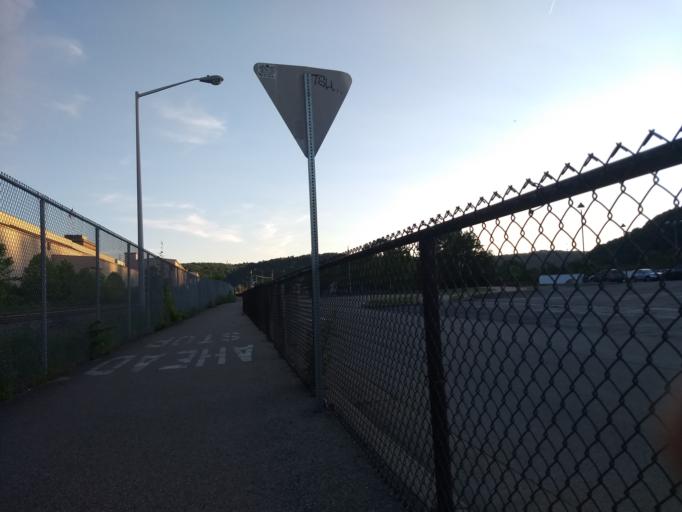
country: US
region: Pennsylvania
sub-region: Allegheny County
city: Homestead
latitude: 40.4018
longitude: -79.9213
